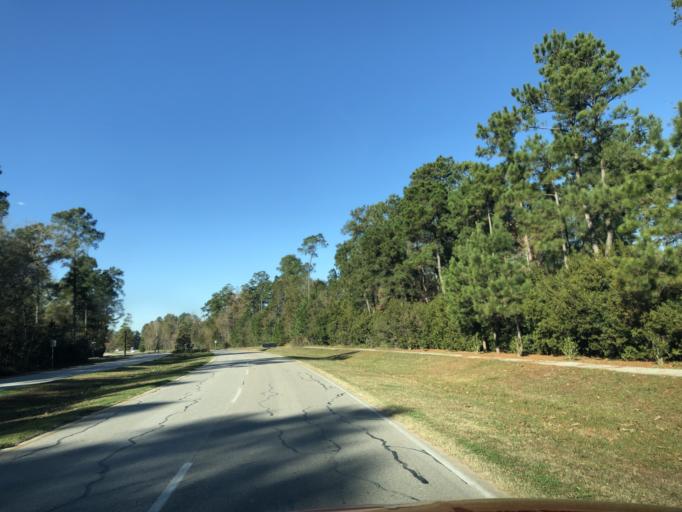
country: US
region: Texas
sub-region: Montgomery County
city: Porter Heights
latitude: 30.0872
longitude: -95.3369
